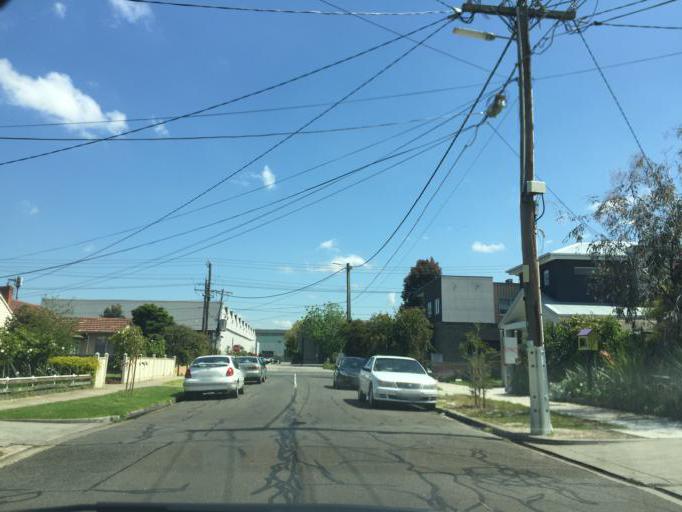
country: AU
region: Victoria
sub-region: Maribyrnong
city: Braybrook
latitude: -37.7914
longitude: 144.8643
